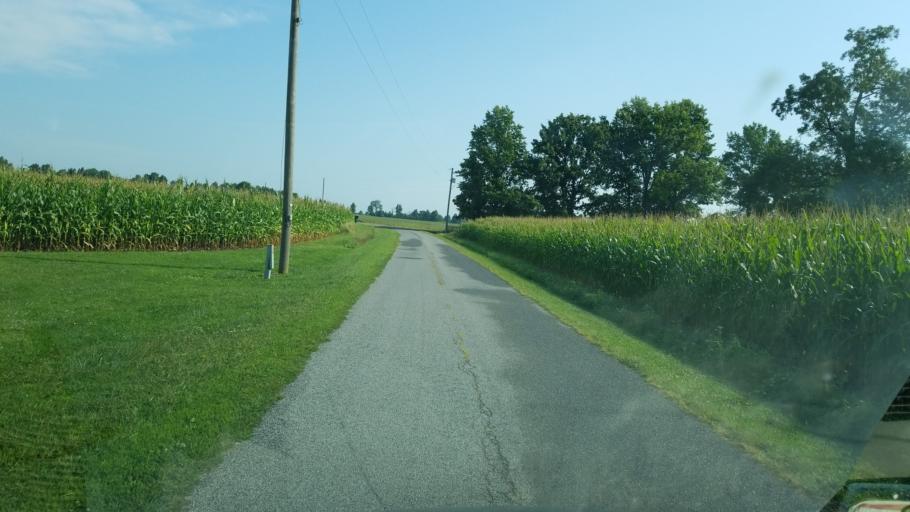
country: US
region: Ohio
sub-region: Crawford County
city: Crestline
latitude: 40.8166
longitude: -82.7739
